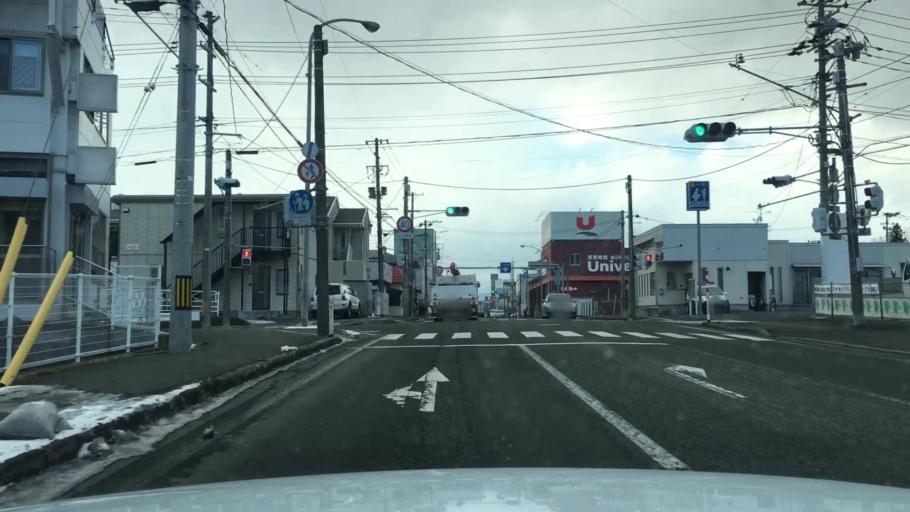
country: JP
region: Iwate
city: Morioka-shi
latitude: 39.6913
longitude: 141.1731
